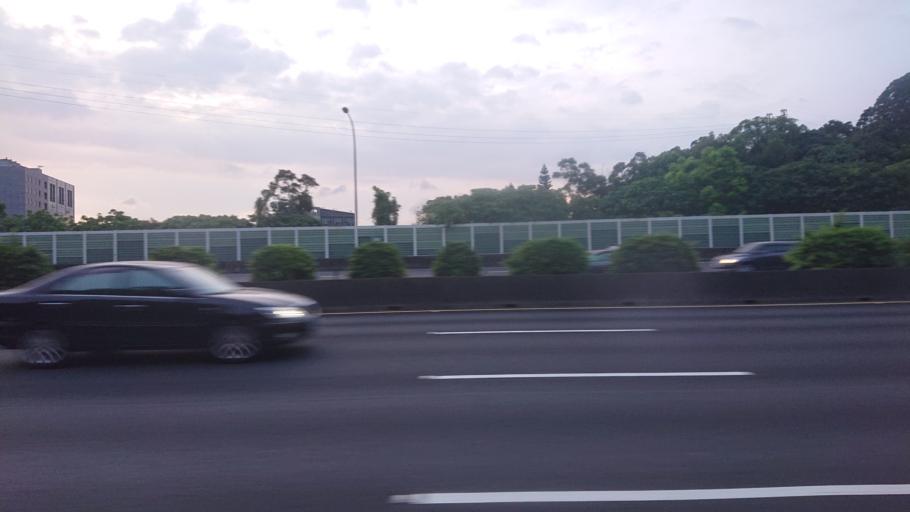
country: TW
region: Taipei
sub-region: Taipei
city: Banqiao
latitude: 24.9588
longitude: 121.4235
